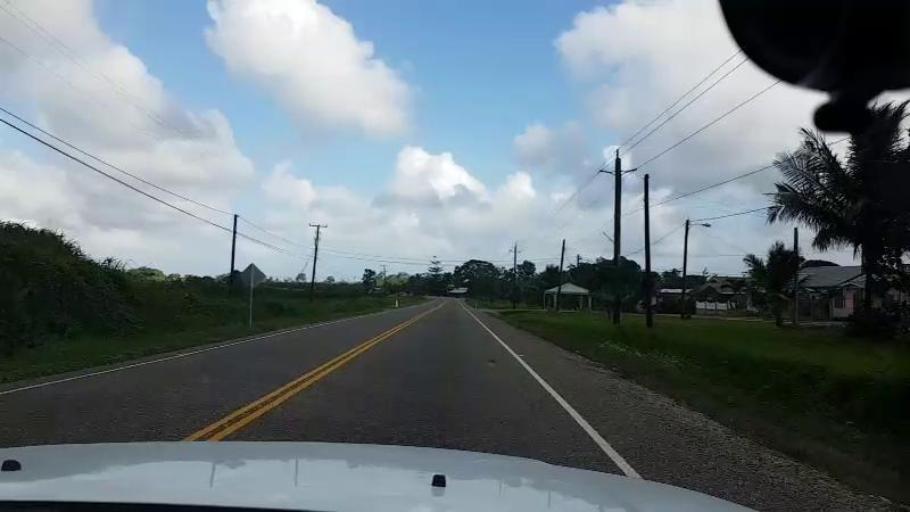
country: BZ
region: Stann Creek
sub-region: Dangriga
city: Dangriga
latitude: 16.9947
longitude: -88.3650
